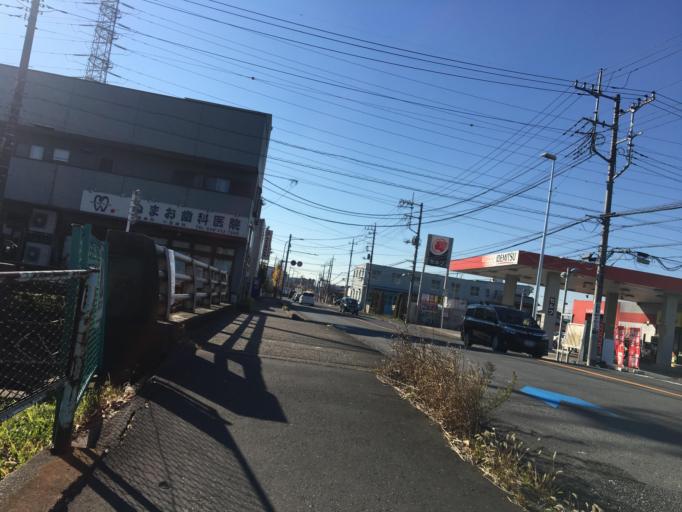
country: JP
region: Saitama
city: Yashio-shi
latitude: 35.8452
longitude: 139.8315
